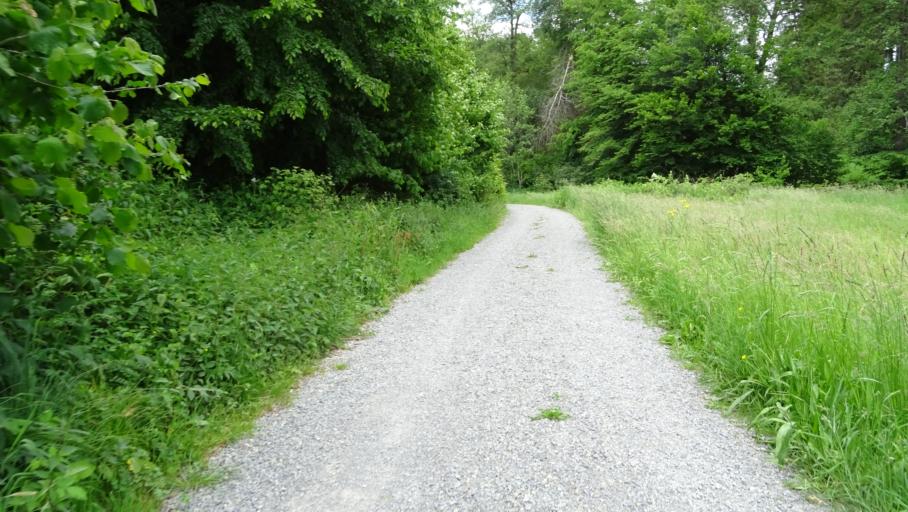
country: DE
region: Baden-Wuerttemberg
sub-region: Karlsruhe Region
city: Mosbach
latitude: 49.3914
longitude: 9.1737
